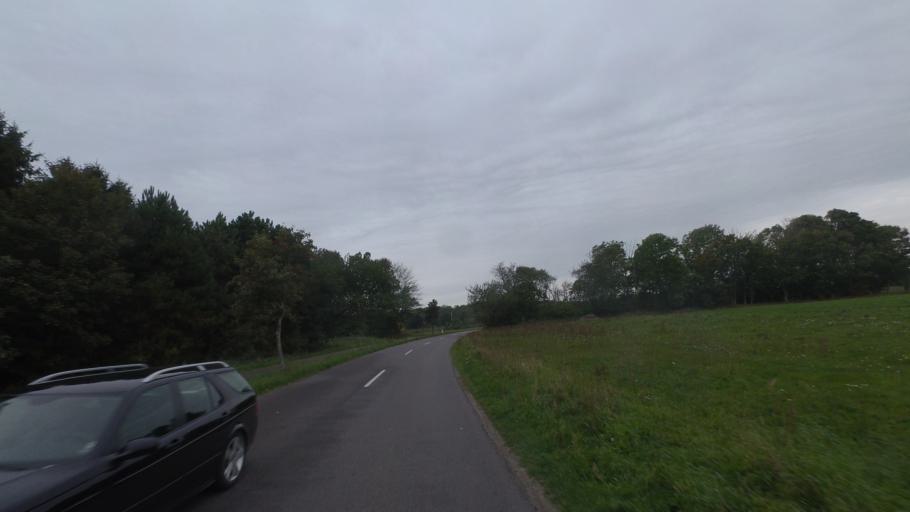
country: DK
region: Capital Region
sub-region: Bornholm Kommune
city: Akirkeby
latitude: 55.0019
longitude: 15.0034
